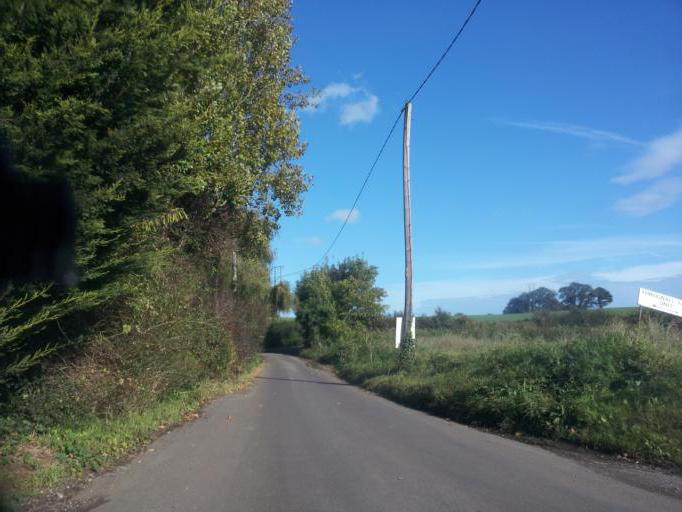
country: GB
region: England
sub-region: Kent
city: Newington
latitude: 51.3417
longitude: 0.6600
